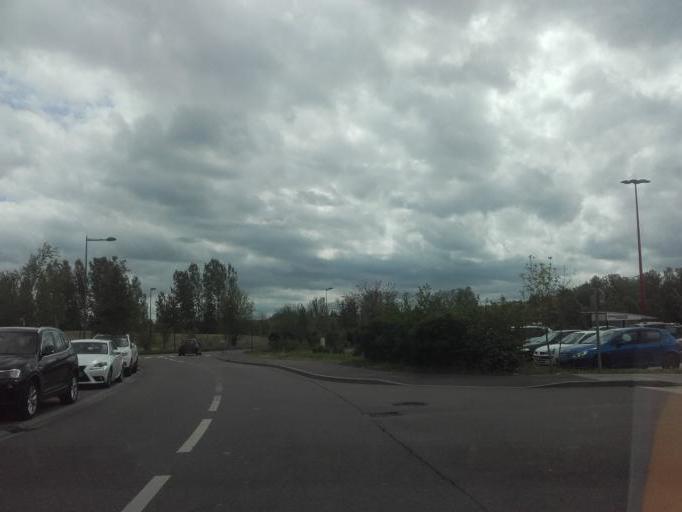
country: FR
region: Bourgogne
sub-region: Departement de Saone-et-Loire
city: Saint-Remy
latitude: 46.7761
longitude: 4.8380
